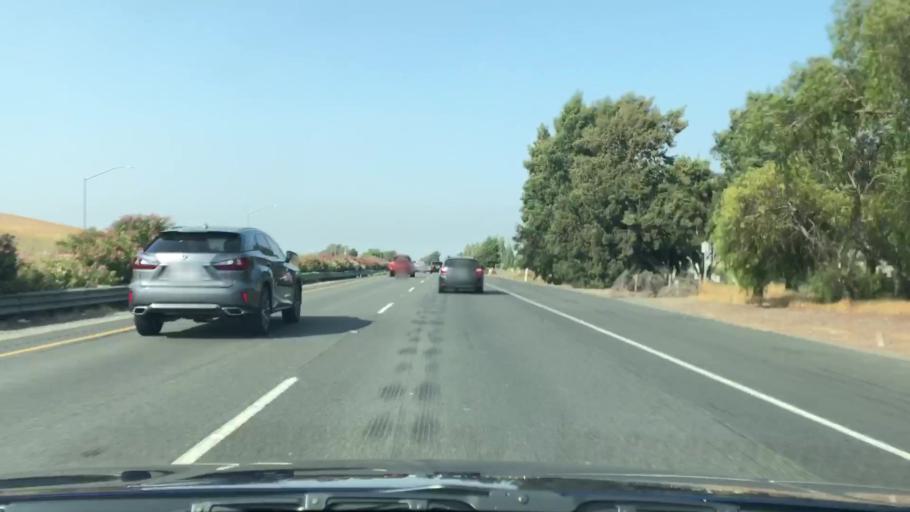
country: US
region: California
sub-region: Solano County
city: Benicia
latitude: 38.0868
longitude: -122.1106
